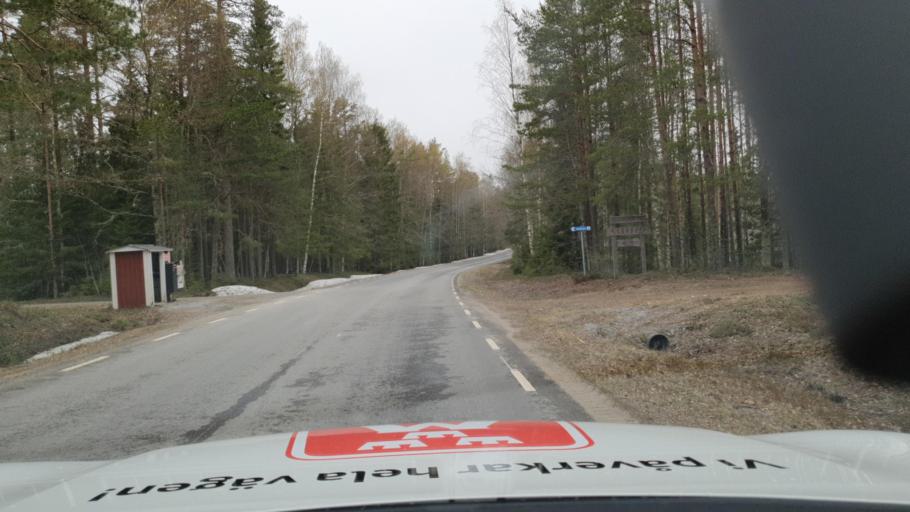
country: SE
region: Vaesterbotten
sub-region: Nordmalings Kommun
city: Nordmaling
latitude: 63.7032
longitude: 19.6124
